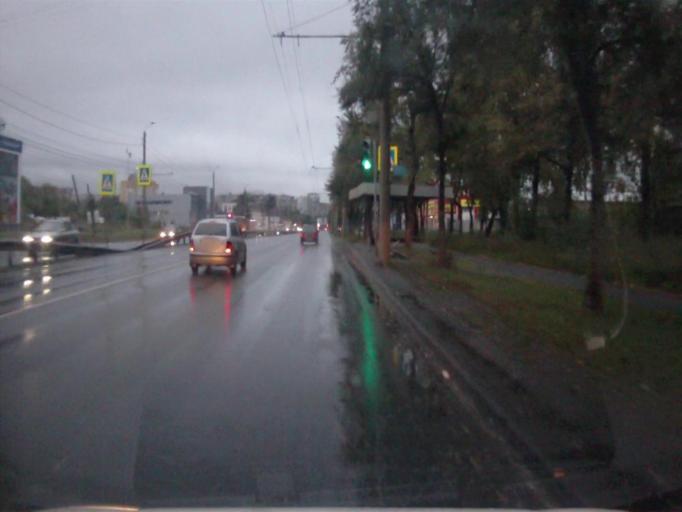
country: RU
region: Chelyabinsk
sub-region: Gorod Chelyabinsk
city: Chelyabinsk
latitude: 55.1369
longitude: 61.4616
